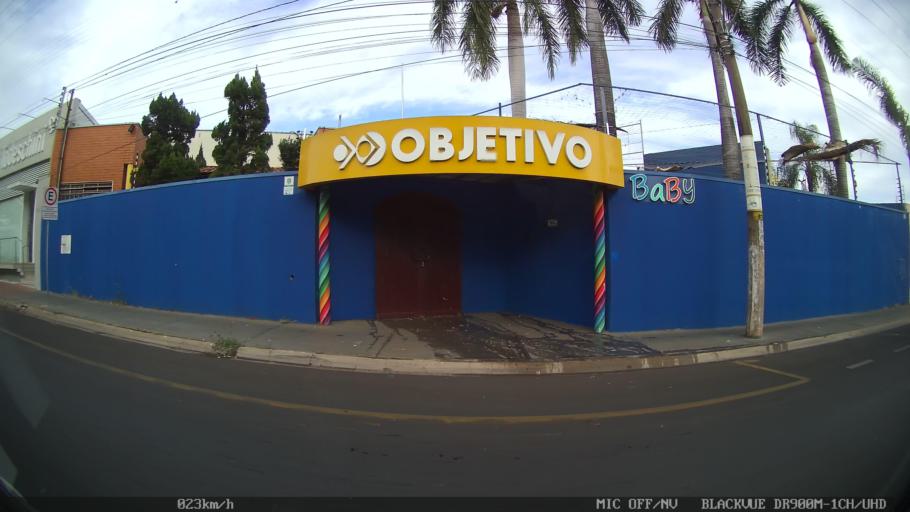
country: BR
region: Sao Paulo
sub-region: Catanduva
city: Catanduva
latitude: -21.1374
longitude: -48.9674
